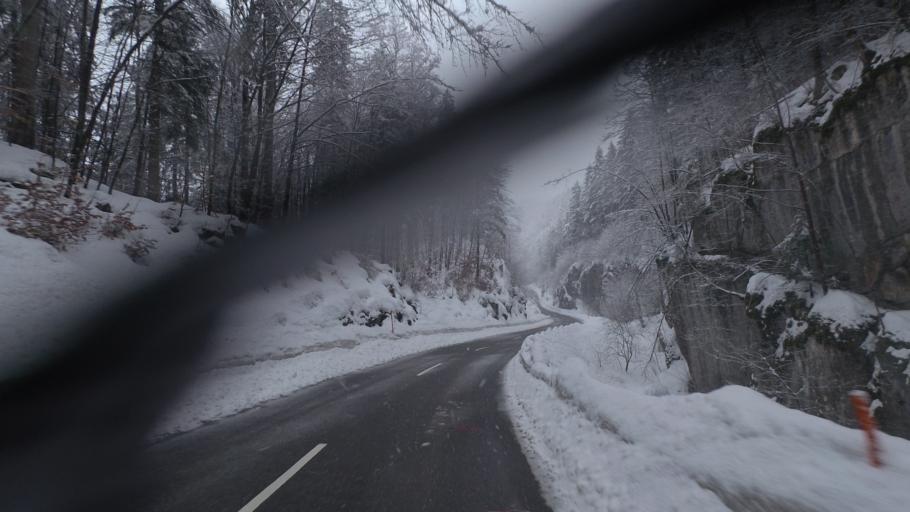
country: DE
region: Bavaria
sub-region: Upper Bavaria
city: Schleching
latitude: 47.7003
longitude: 12.3924
